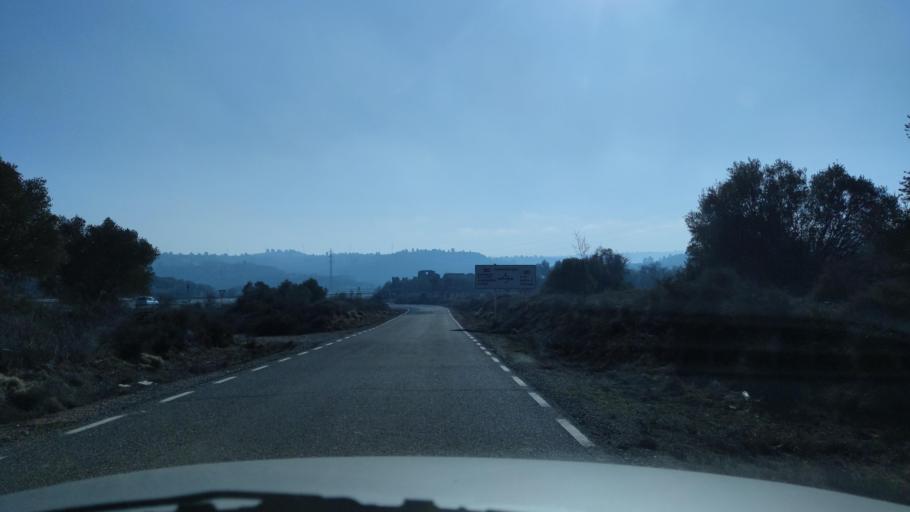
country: ES
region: Catalonia
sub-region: Provincia de Lleida
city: Torrebesses
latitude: 41.4278
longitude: 0.5851
